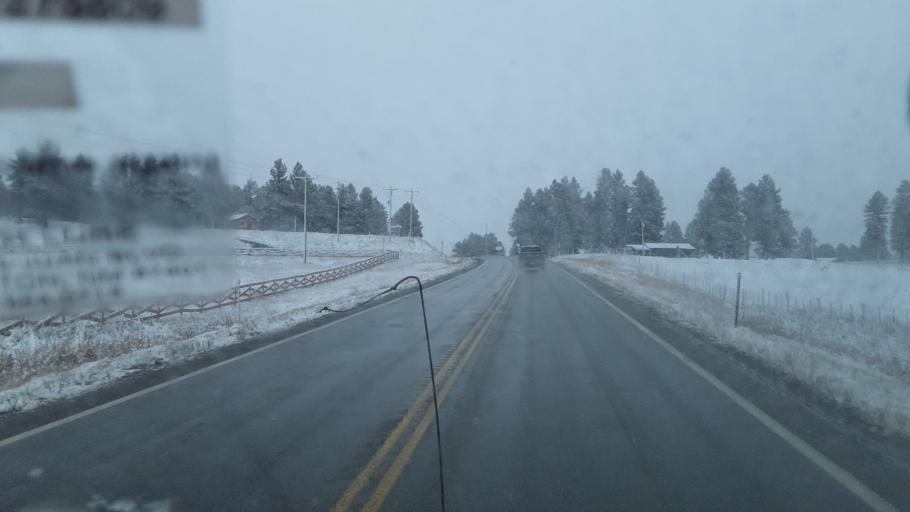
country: US
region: Colorado
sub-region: Archuleta County
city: Pagosa Springs
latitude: 37.2310
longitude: -106.9847
